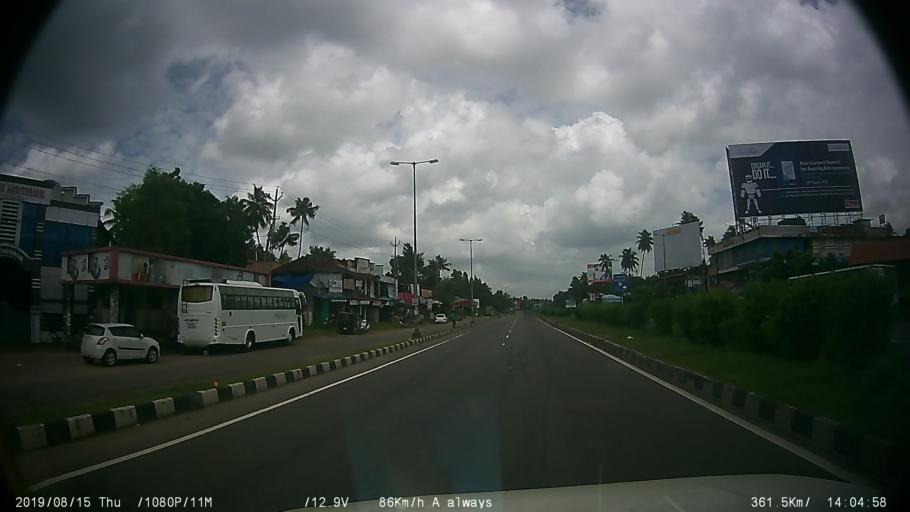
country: IN
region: Kerala
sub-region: Thrissur District
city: Irinjalakuda
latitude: 10.4059
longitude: 76.2762
